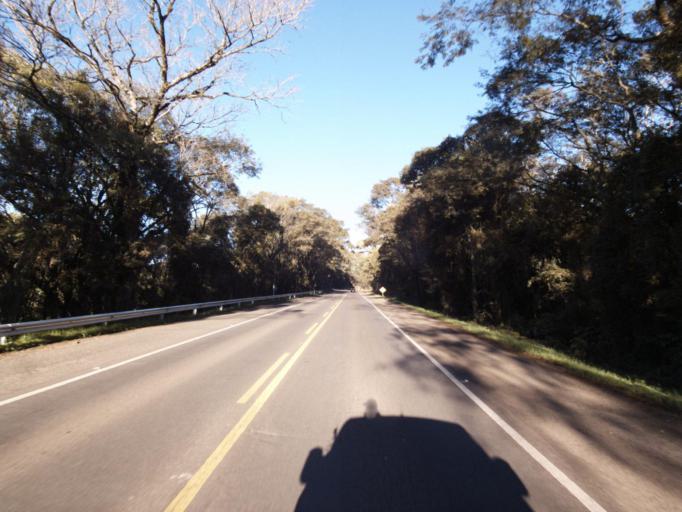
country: BR
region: Santa Catarina
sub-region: Sao Lourenco Do Oeste
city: Sao Lourenco dOeste
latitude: -26.7679
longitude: -53.2612
